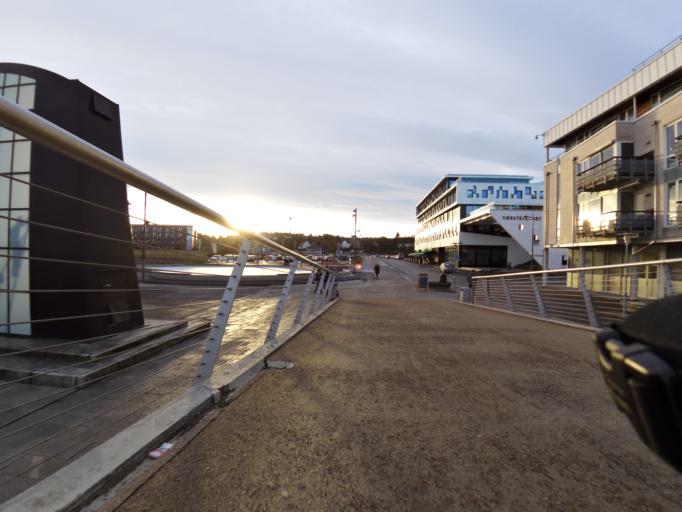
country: NO
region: Ostfold
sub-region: Fredrikstad
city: Fredrikstad
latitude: 59.2123
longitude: 10.9335
